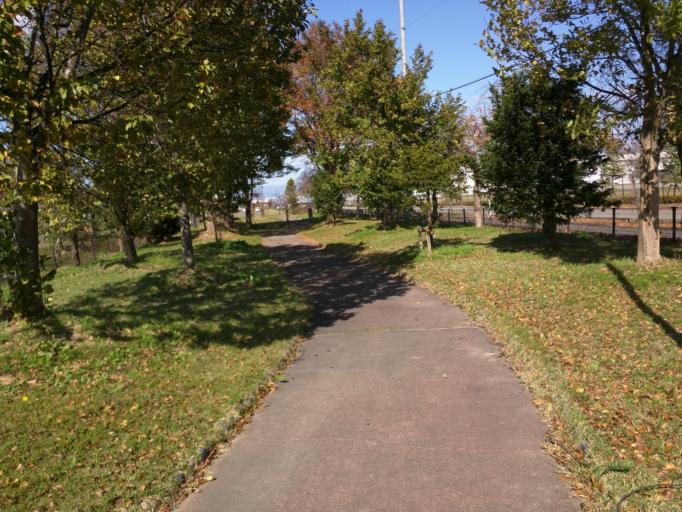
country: JP
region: Fukushima
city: Kitakata
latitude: 37.5418
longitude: 139.8777
